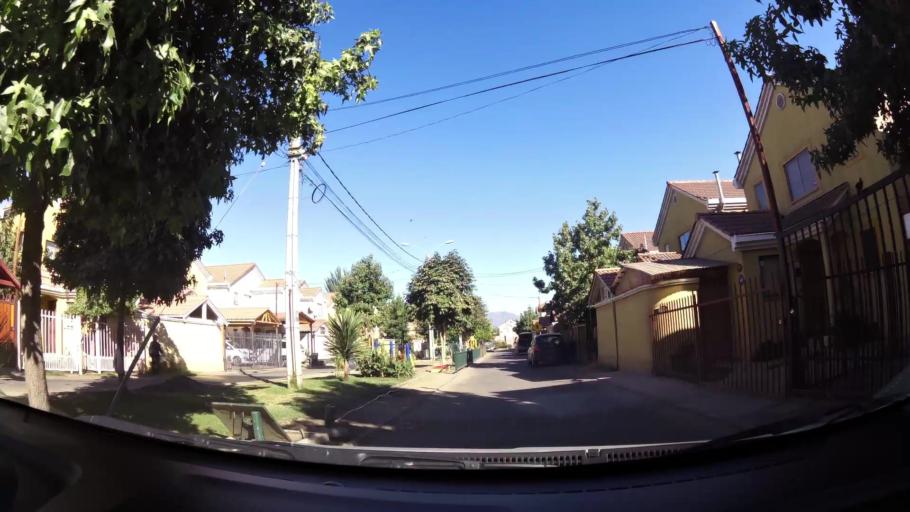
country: CL
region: O'Higgins
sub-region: Provincia de Cachapoal
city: Rancagua
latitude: -34.1876
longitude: -70.7268
